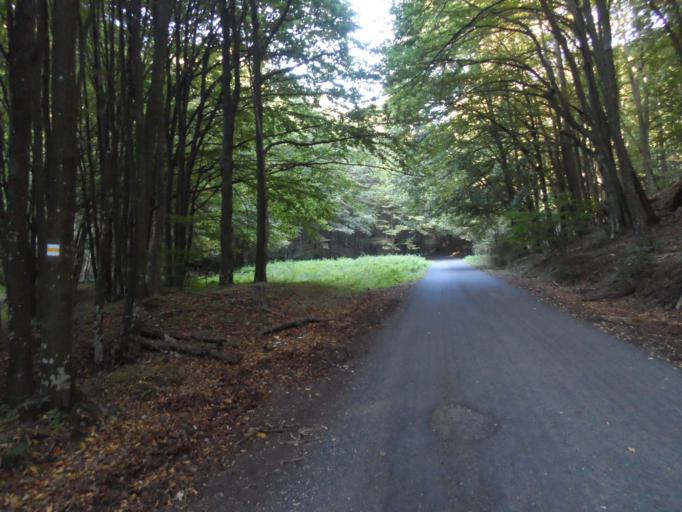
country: HU
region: Veszprem
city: Zirc
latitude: 47.2720
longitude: 17.7586
